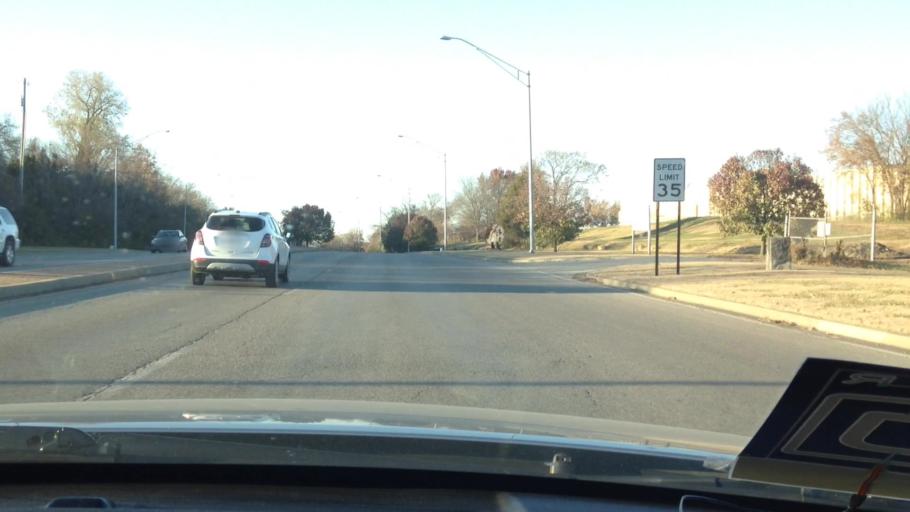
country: US
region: Kansas
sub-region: Johnson County
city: Roeland Park
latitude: 39.0411
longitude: -94.6410
